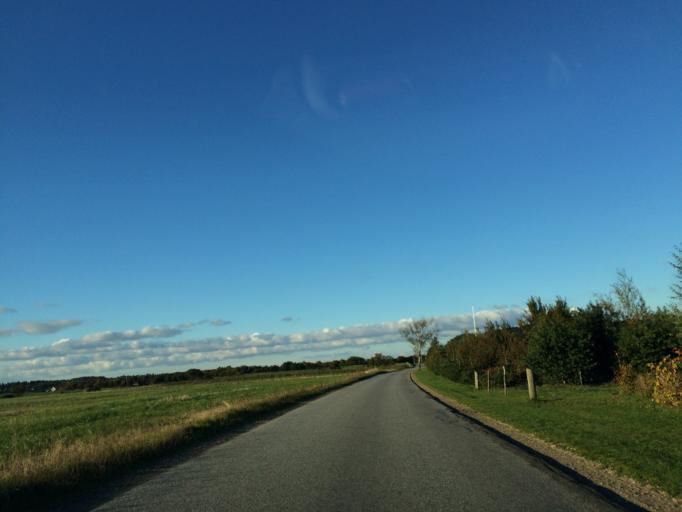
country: DK
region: Central Jutland
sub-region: Silkeborg Kommune
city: Svejbaek
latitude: 56.1800
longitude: 9.6920
